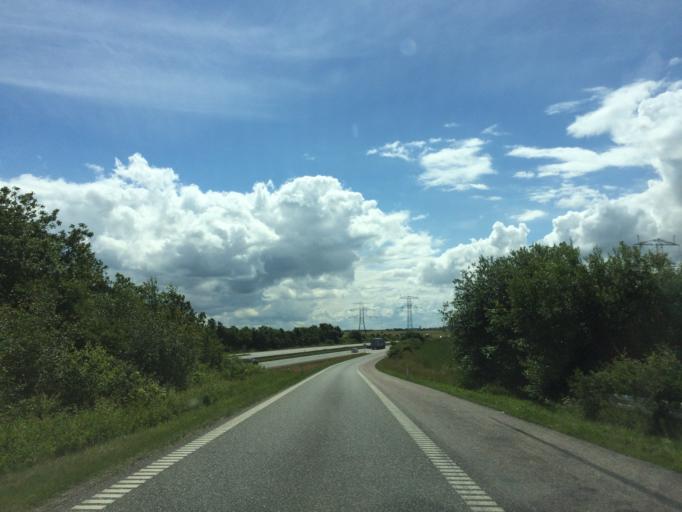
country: DK
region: North Denmark
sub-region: Rebild Kommune
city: Stovring
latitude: 56.8796
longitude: 9.8019
